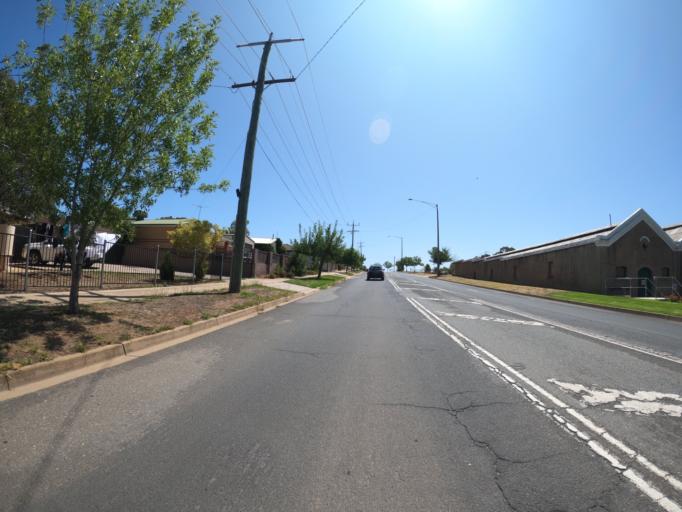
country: AU
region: New South Wales
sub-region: Corowa Shire
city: Corowa
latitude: -36.0523
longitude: 146.4547
